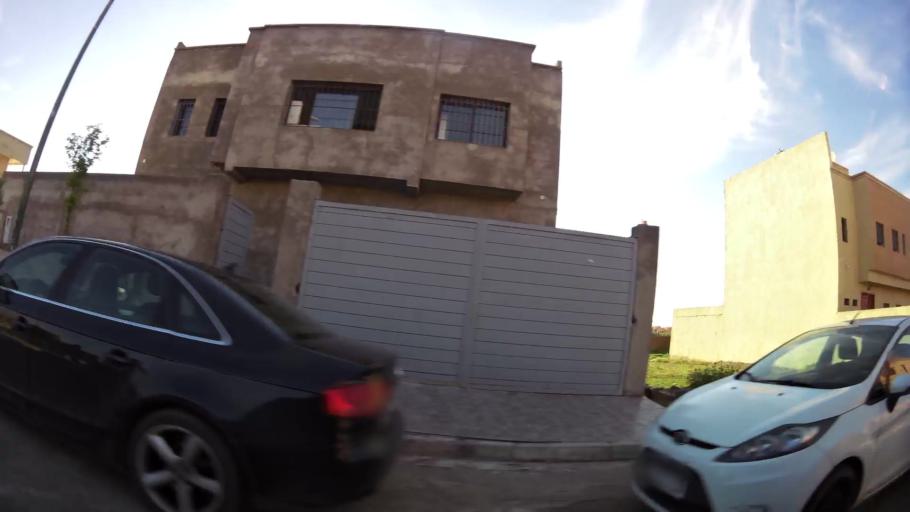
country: MA
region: Marrakech-Tensift-Al Haouz
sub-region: Marrakech
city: Marrakesh
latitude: 31.6804
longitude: -8.0642
